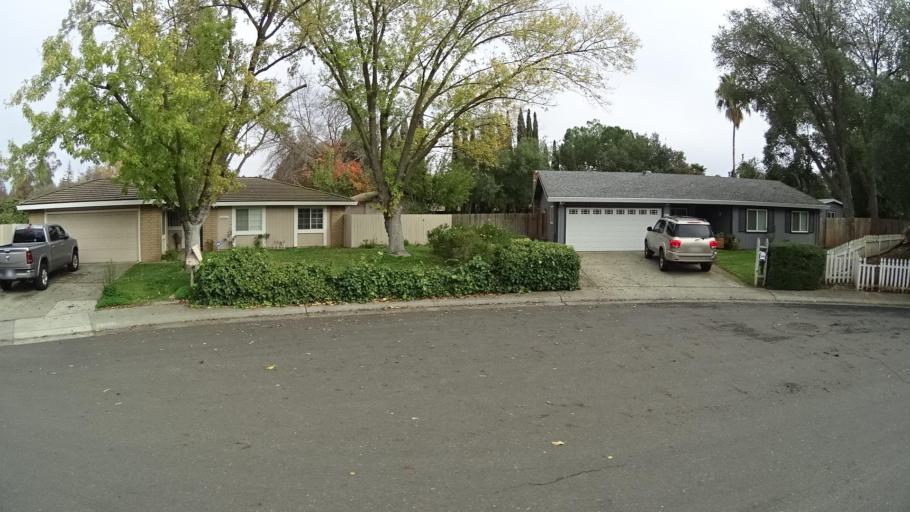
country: US
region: California
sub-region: Sacramento County
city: Elk Grove
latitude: 38.4119
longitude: -121.3671
